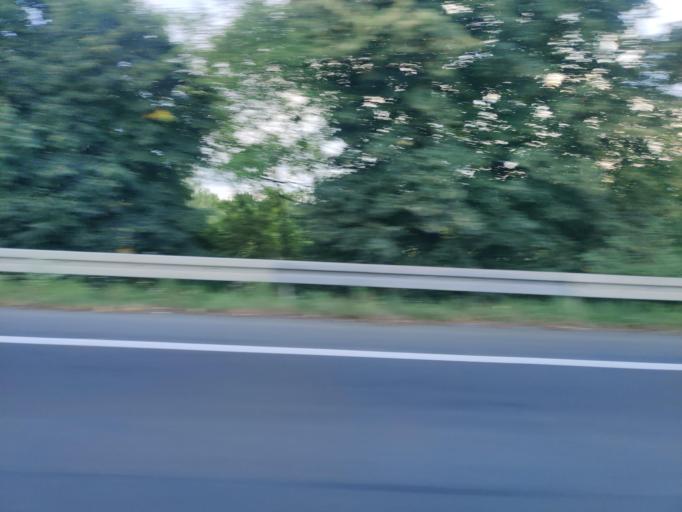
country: PL
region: Greater Poland Voivodeship
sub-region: Konin
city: Konin
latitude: 52.2082
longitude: 18.2649
